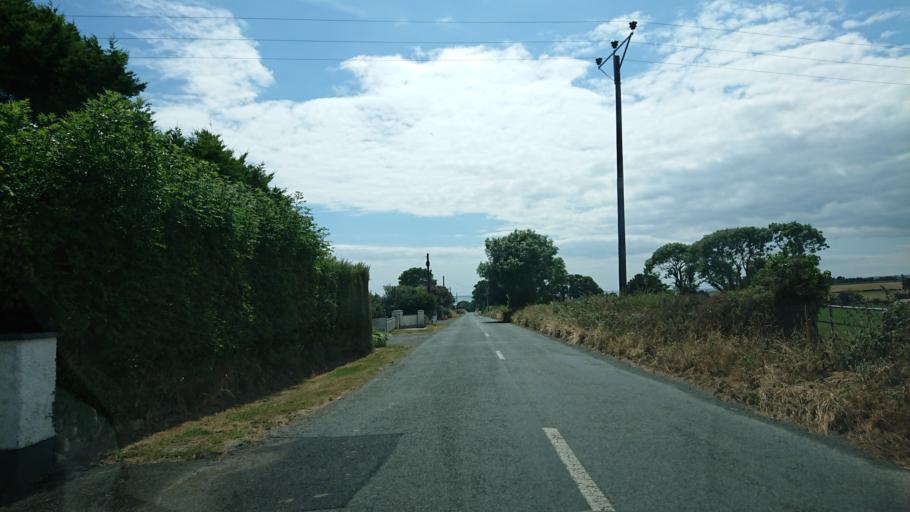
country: IE
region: Munster
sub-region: Waterford
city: Portlaw
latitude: 52.1506
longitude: -7.3526
